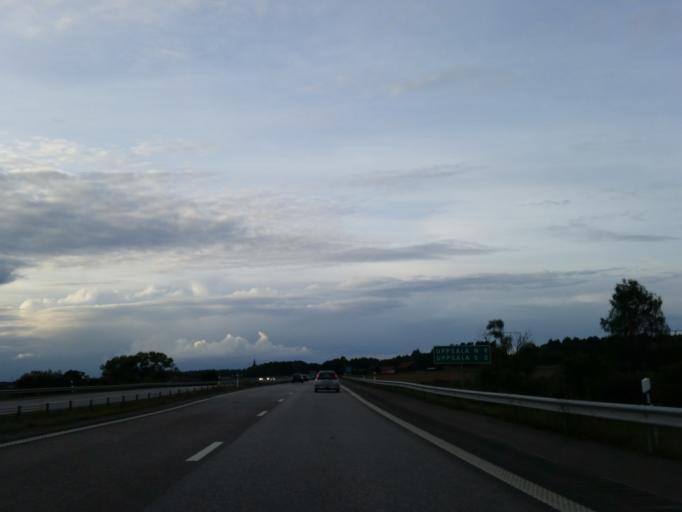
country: SE
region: Uppsala
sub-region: Uppsala Kommun
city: Saevja
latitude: 59.8139
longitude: 17.7555
